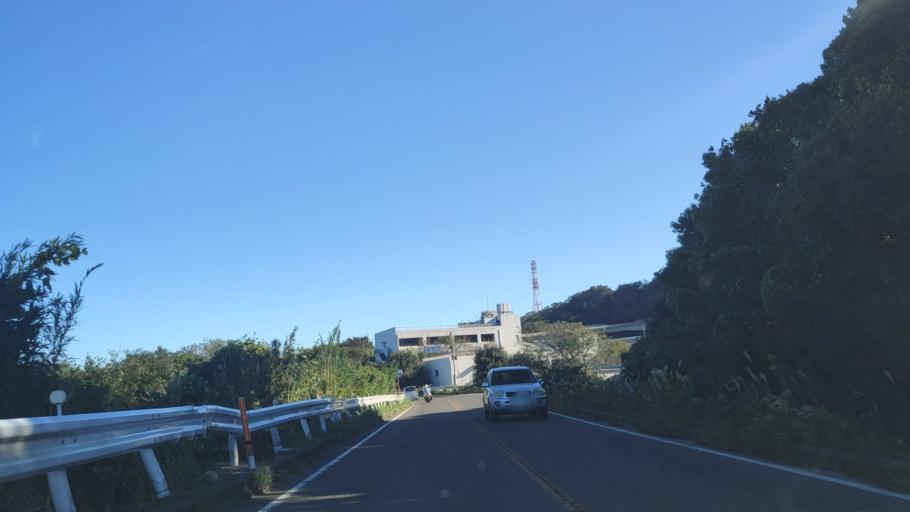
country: JP
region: Kanagawa
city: Zama
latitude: 35.5268
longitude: 139.3527
